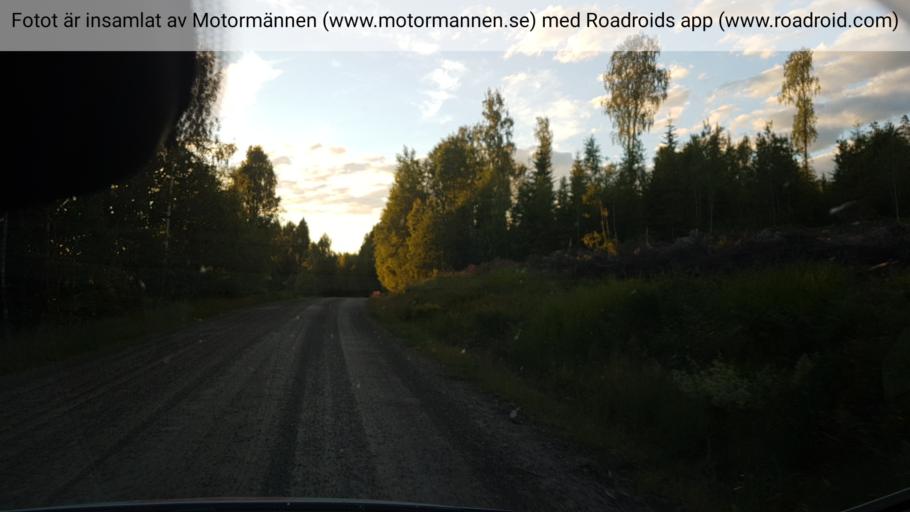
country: SE
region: Vaermland
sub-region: Sunne Kommun
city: Sunne
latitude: 59.6738
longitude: 12.9021
